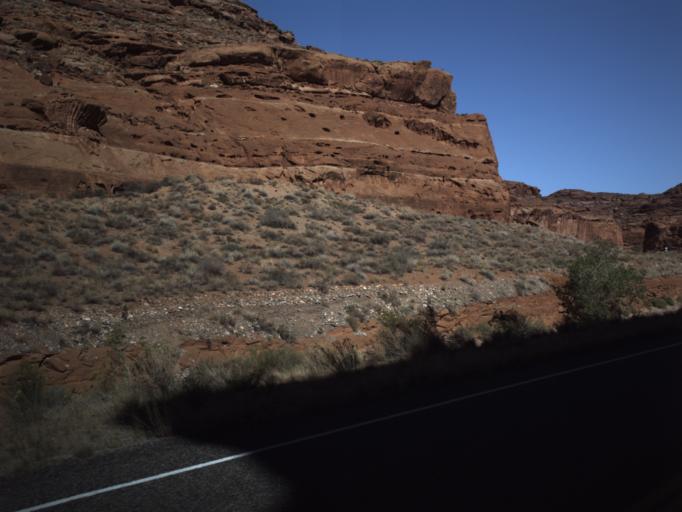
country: US
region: Utah
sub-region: San Juan County
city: Blanding
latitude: 37.9802
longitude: -110.4923
